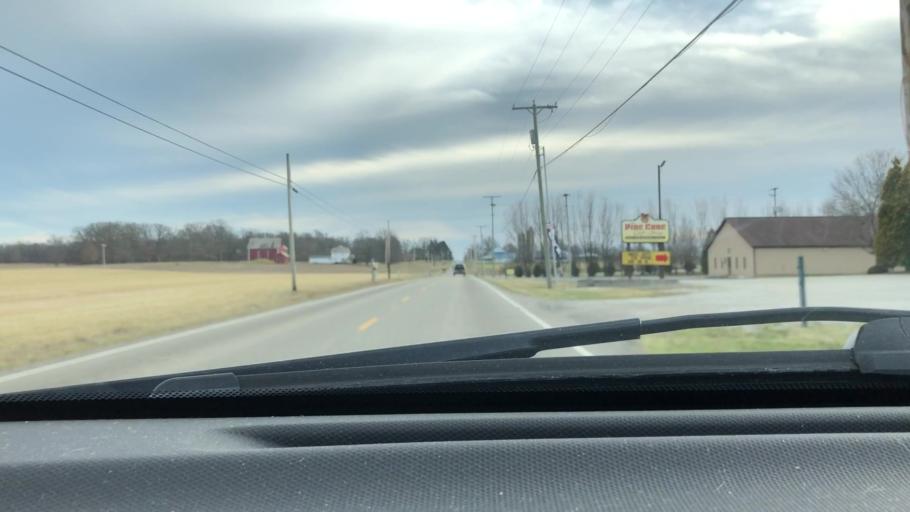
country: US
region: Ohio
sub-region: Wayne County
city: Dalton
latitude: 40.7657
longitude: -81.7453
